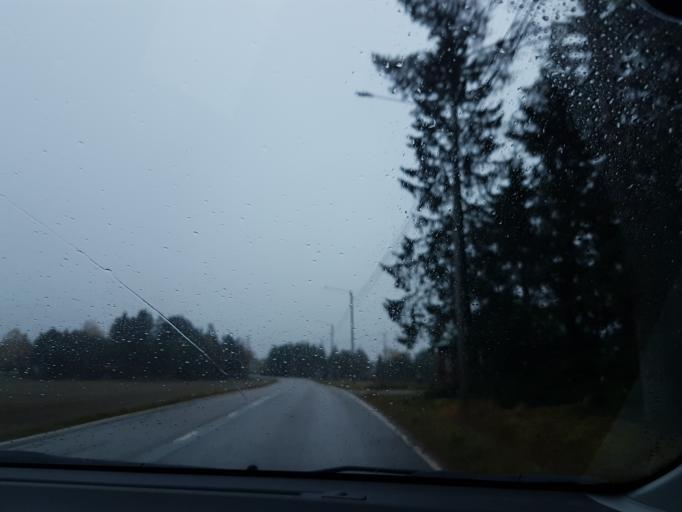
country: FI
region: Uusimaa
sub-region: Helsinki
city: Maentsaelae
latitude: 60.6182
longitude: 25.2543
